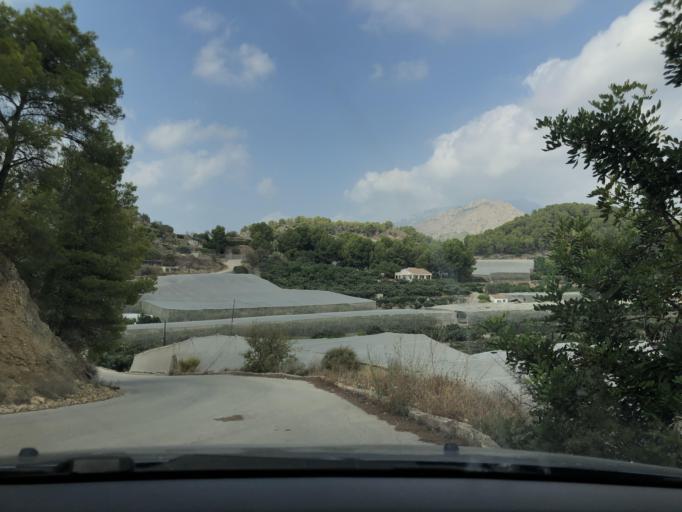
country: ES
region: Valencia
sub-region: Provincia de Alicante
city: Callosa d'En Sarria
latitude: 38.6364
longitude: -0.1128
